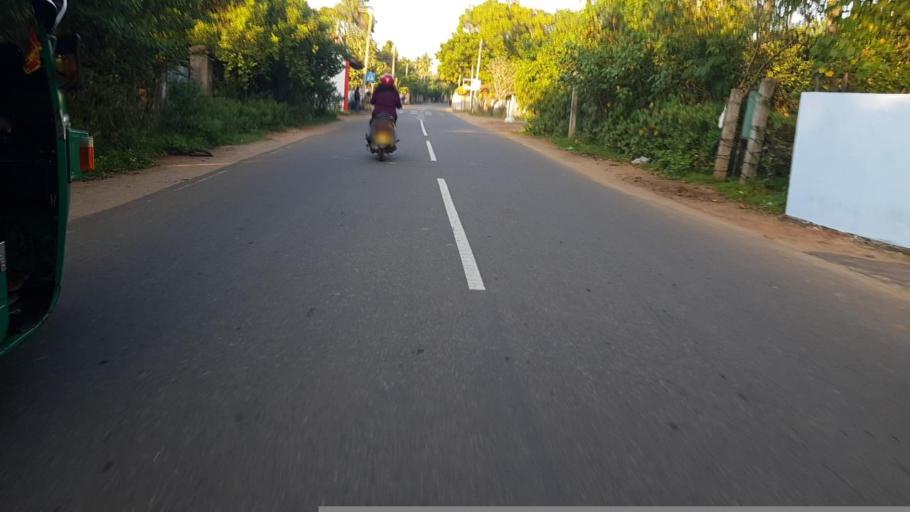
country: LK
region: Northern Province
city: Jaffna
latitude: 9.7319
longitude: 79.9507
